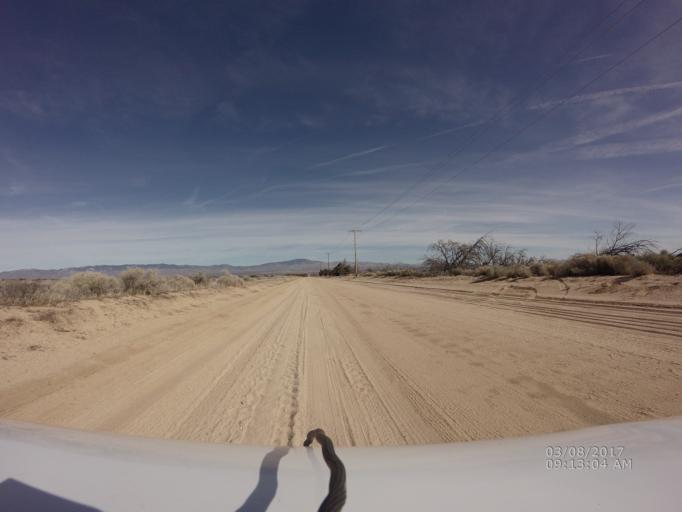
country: US
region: California
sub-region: Los Angeles County
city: Green Valley
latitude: 34.7572
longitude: -118.4666
